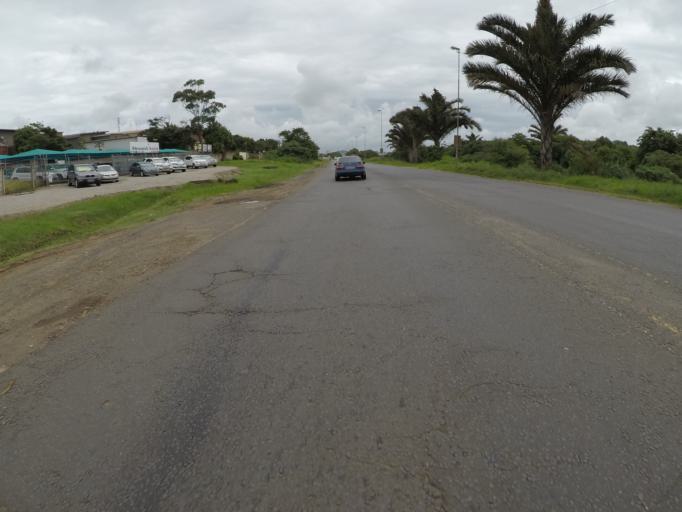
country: ZA
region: KwaZulu-Natal
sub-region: uThungulu District Municipality
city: Empangeni
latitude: -28.7651
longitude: 31.9064
